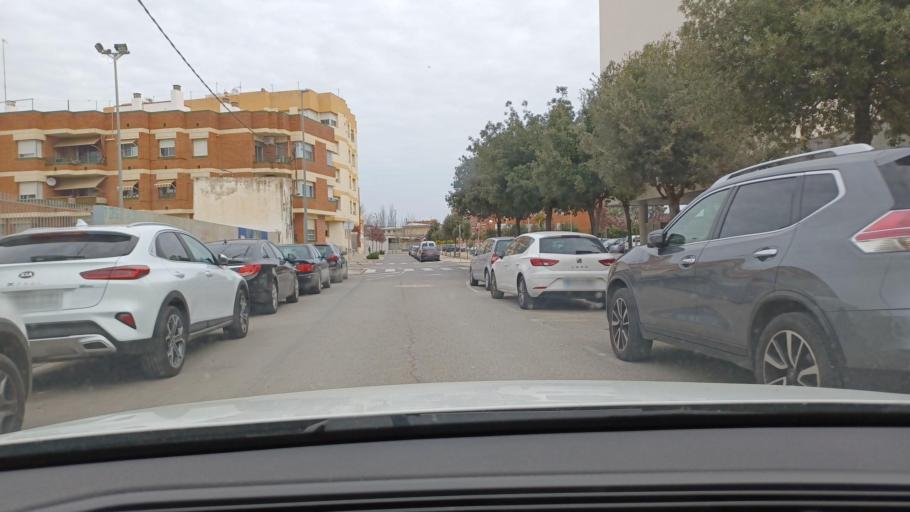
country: ES
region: Catalonia
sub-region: Provincia de Tarragona
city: Amposta
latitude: 40.7080
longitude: 0.5821
